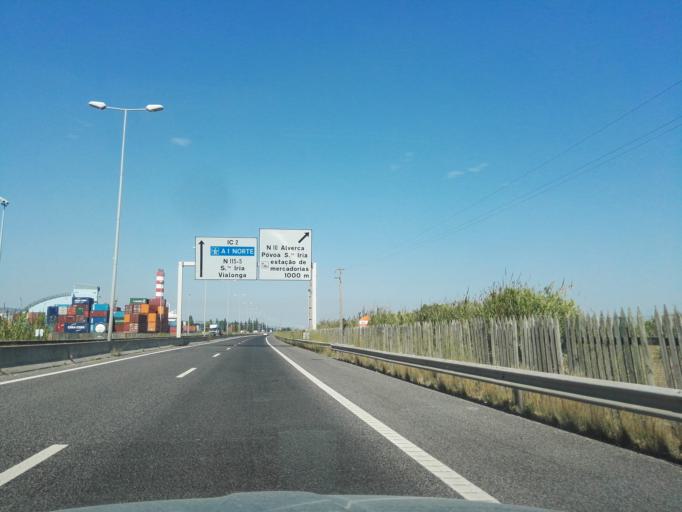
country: PT
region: Lisbon
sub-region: Loures
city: Sao Joao da Talha
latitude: 38.8226
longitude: -9.0846
